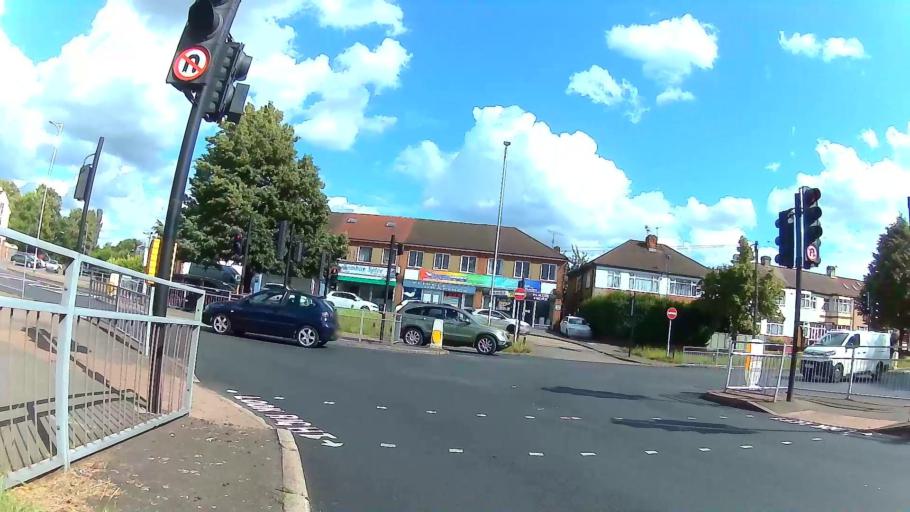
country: GB
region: England
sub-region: Greater London
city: Woodford Green
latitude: 51.6009
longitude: 0.0429
